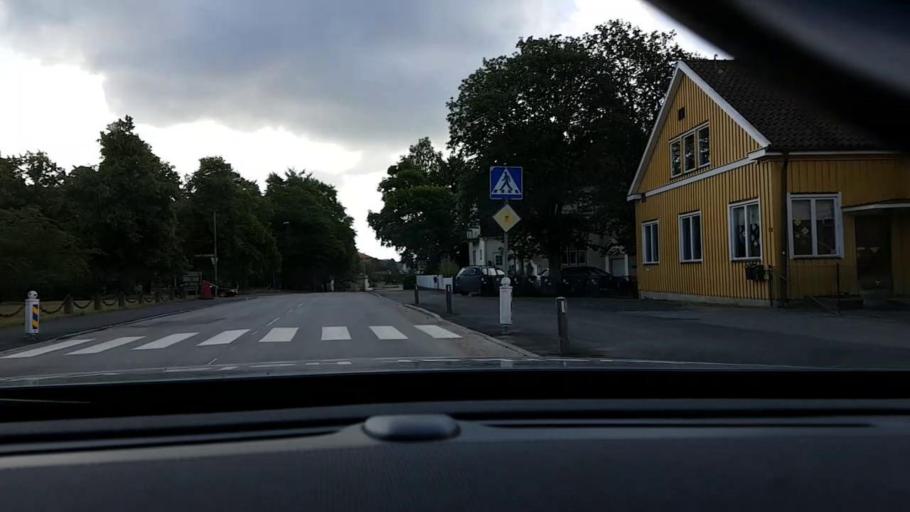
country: SE
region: Skane
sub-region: Hassleholms Kommun
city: Hassleholm
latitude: 56.1650
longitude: 13.7552
